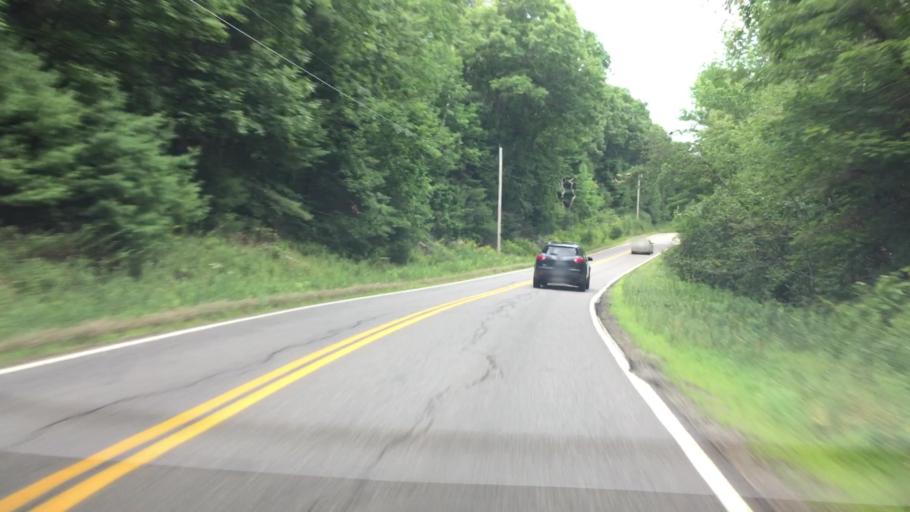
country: US
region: Maine
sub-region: Waldo County
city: Lincolnville
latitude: 44.3503
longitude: -69.0553
